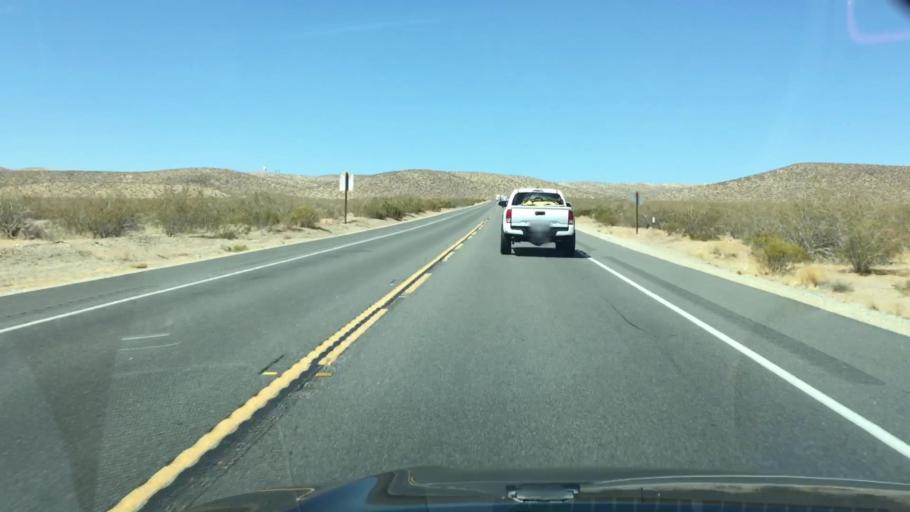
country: US
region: California
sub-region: Kern County
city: Ridgecrest
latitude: 35.4273
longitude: -117.6724
